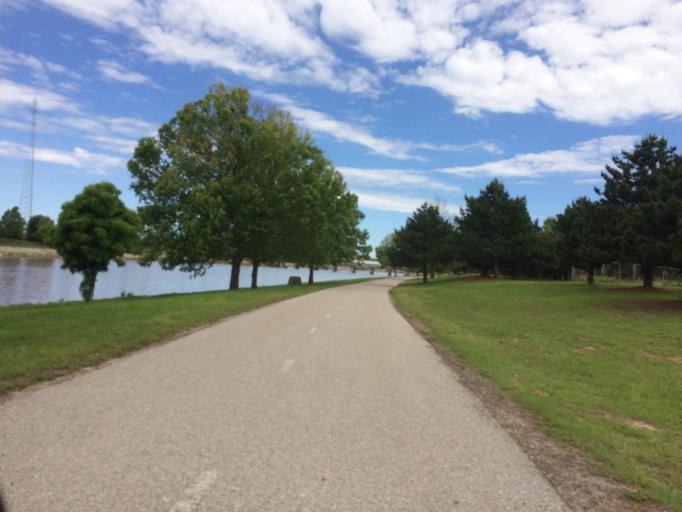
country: US
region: Oklahoma
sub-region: Oklahoma County
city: Oklahoma City
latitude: 35.4521
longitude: -97.5077
